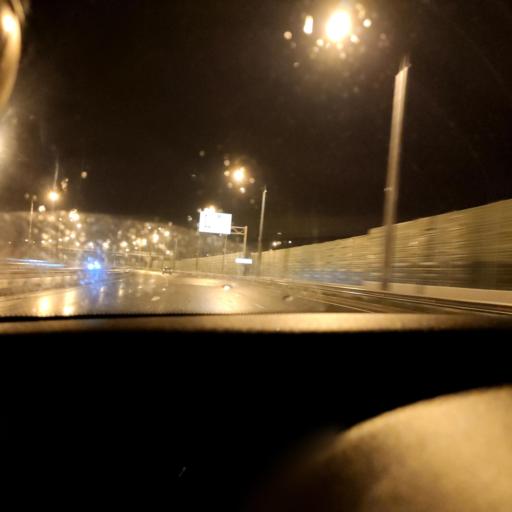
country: RU
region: Samara
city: Samara
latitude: 53.1675
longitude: 50.0853
